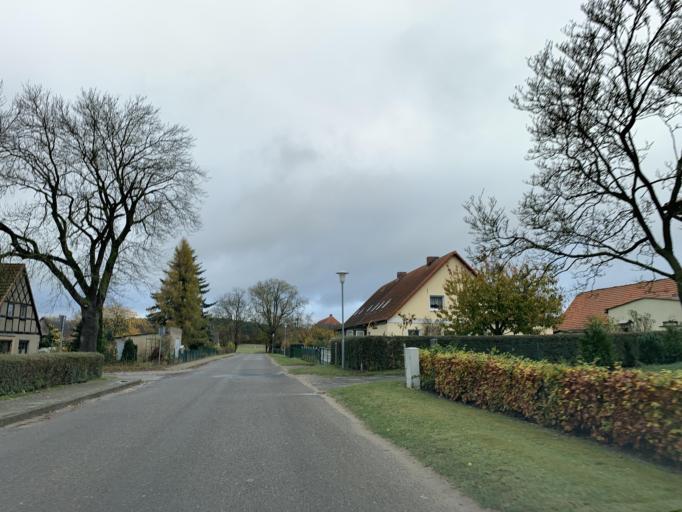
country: DE
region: Mecklenburg-Vorpommern
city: Blankensee
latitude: 53.3840
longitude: 13.2622
